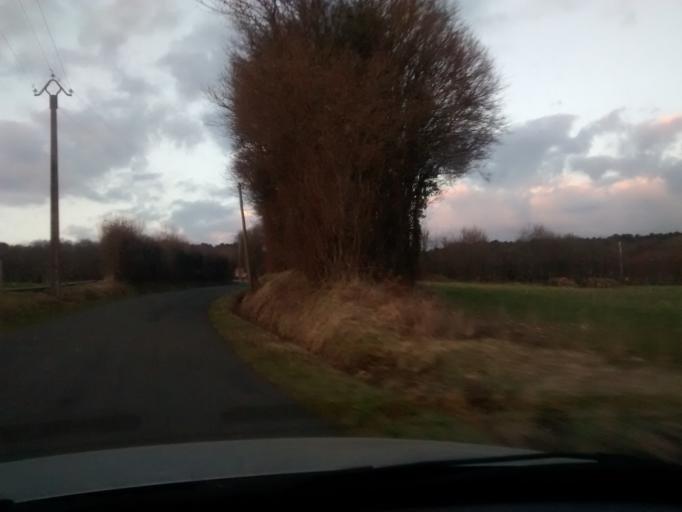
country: FR
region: Pays de la Loire
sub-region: Departement de la Sarthe
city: Challes
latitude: 47.9482
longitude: 0.4367
